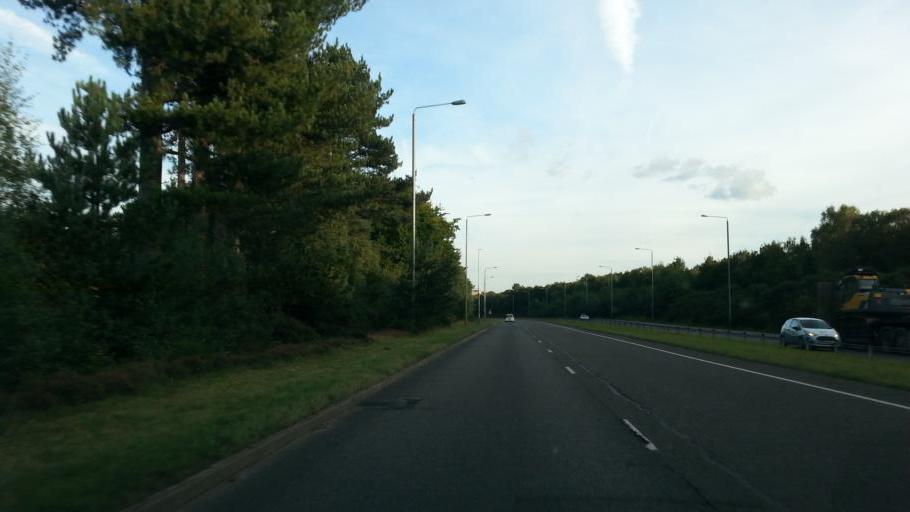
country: GB
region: England
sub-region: Nottinghamshire
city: Rainworth
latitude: 53.1271
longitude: -1.1246
